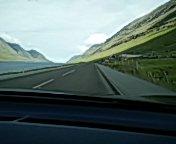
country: FO
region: Nordoyar
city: Klaksvik
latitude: 62.3019
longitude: -6.5229
